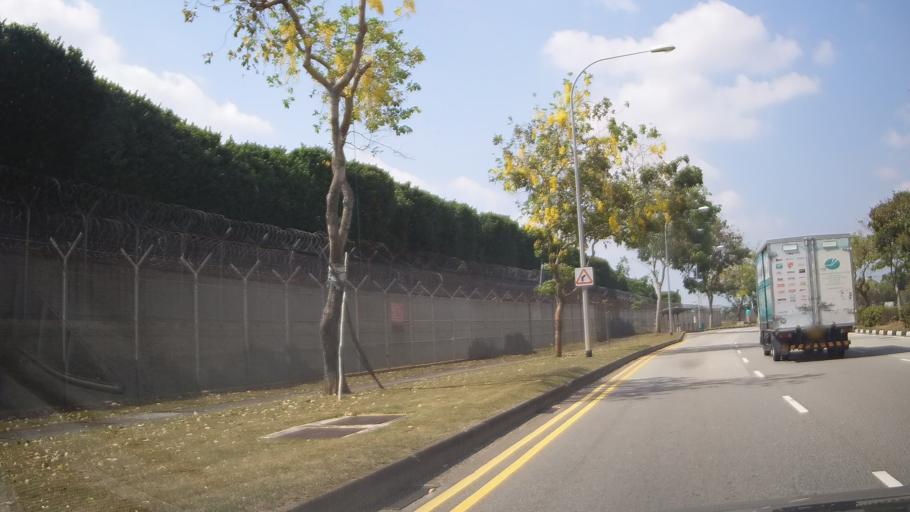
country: SG
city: Singapore
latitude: 1.3660
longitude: 103.9092
